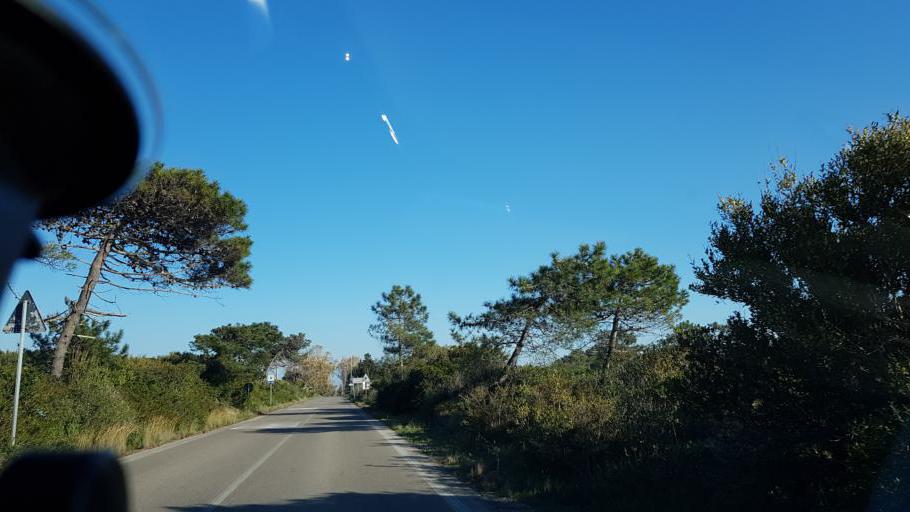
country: IT
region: Apulia
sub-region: Provincia di Lecce
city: Giorgilorio
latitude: 40.4555
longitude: 18.2129
